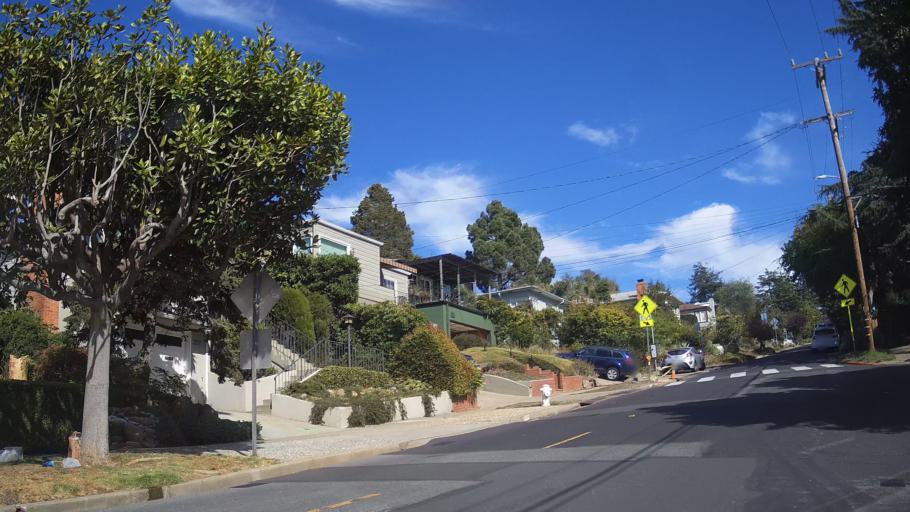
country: US
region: California
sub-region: Contra Costa County
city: Kensington
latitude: 37.9091
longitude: -122.2758
